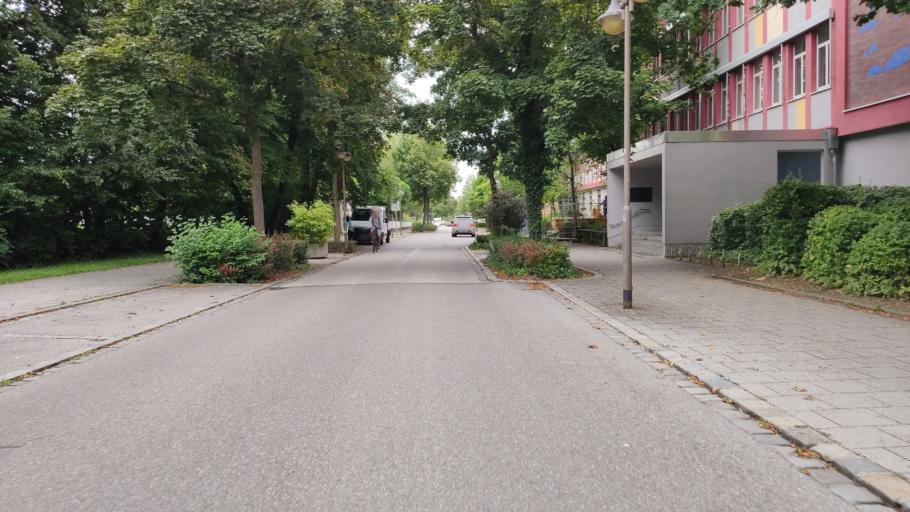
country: DE
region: Bavaria
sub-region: Swabia
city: Konigsbrunn
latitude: 48.2711
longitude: 10.8920
